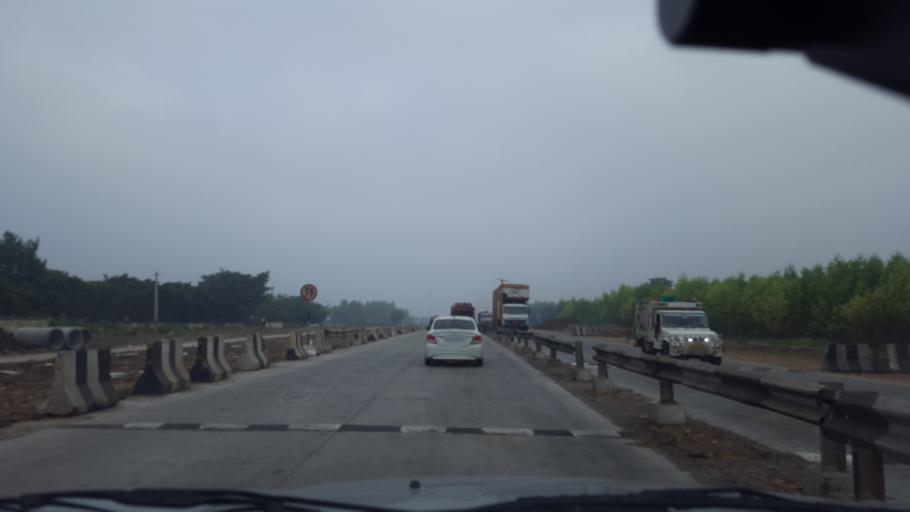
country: IN
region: Andhra Pradesh
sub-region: Prakasam
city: Addanki
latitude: 15.7932
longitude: 80.0386
